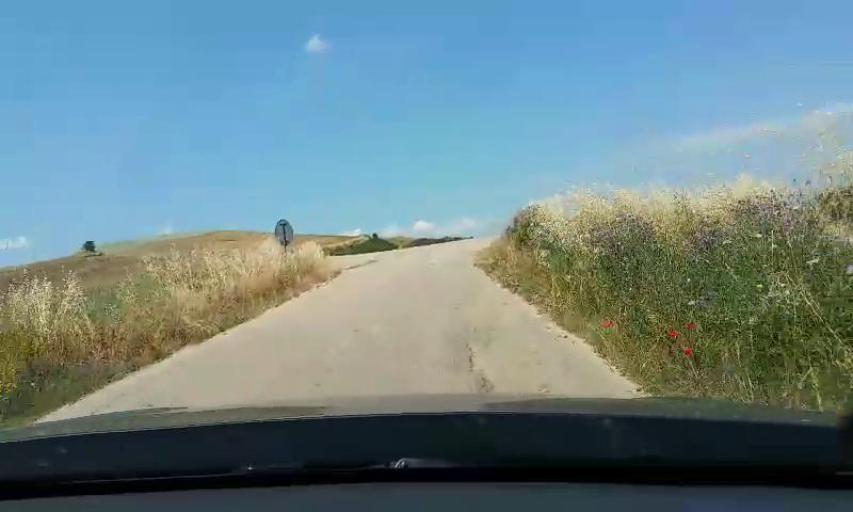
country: IT
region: Molise
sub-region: Provincia di Campobasso
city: Montecilfone
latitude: 41.9243
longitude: 14.8520
